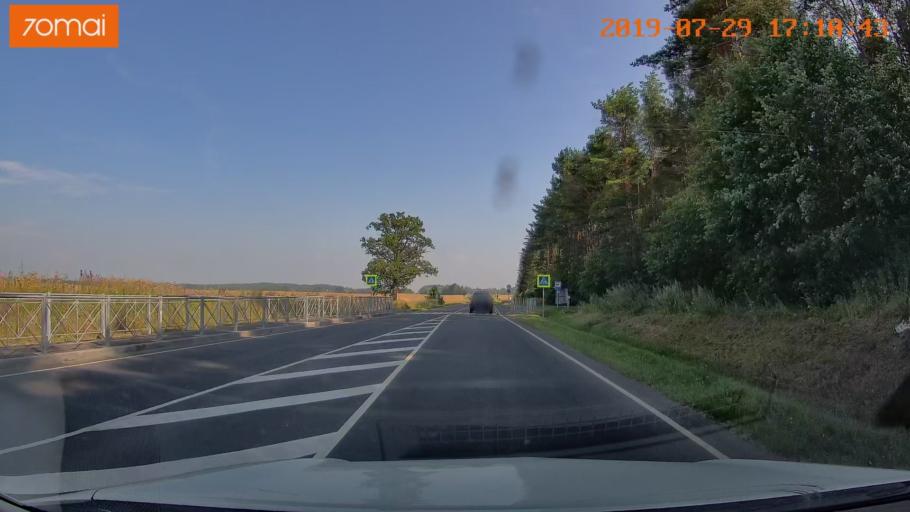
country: RU
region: Kaliningrad
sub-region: Gorod Kaliningrad
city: Kaliningrad
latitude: 54.8002
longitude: 20.3719
